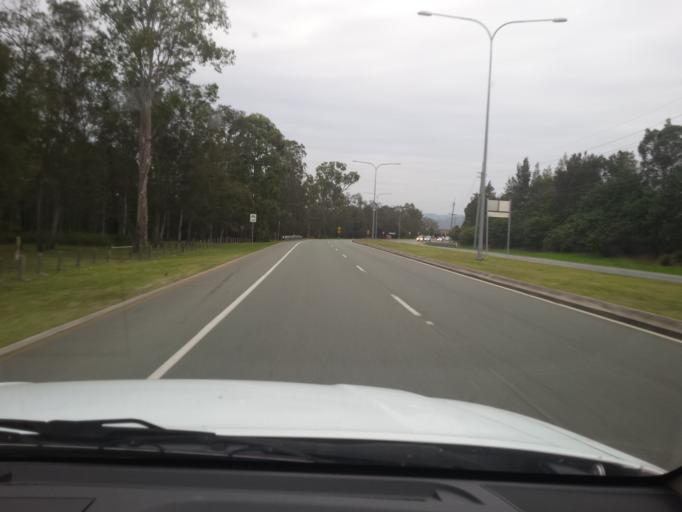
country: AU
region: Queensland
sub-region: Gold Coast
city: Oxenford
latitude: -27.8819
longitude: 153.3279
